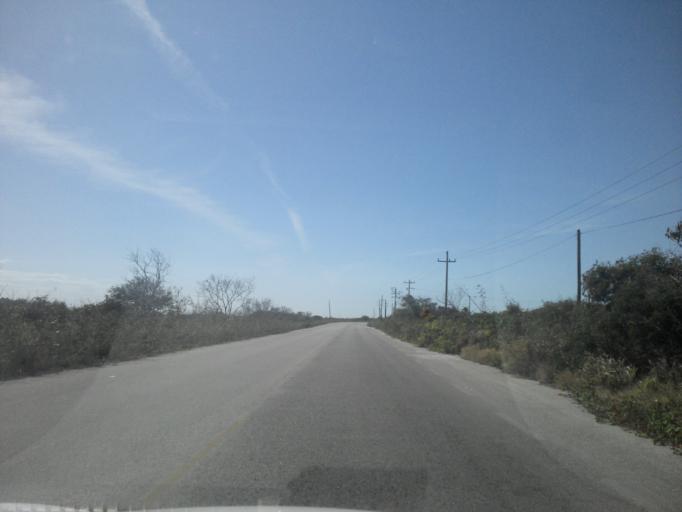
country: MX
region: Yucatan
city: Telchac Puerto
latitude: 21.3318
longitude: -89.3587
